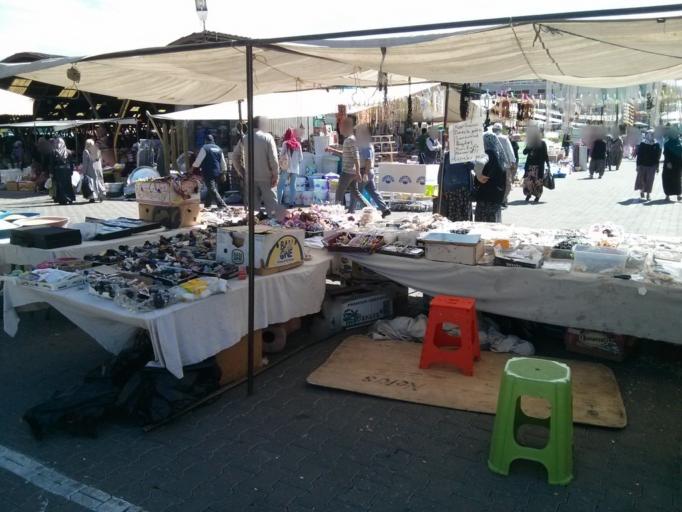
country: TR
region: Nevsehir
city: Avanos
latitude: 38.7147
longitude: 34.8446
